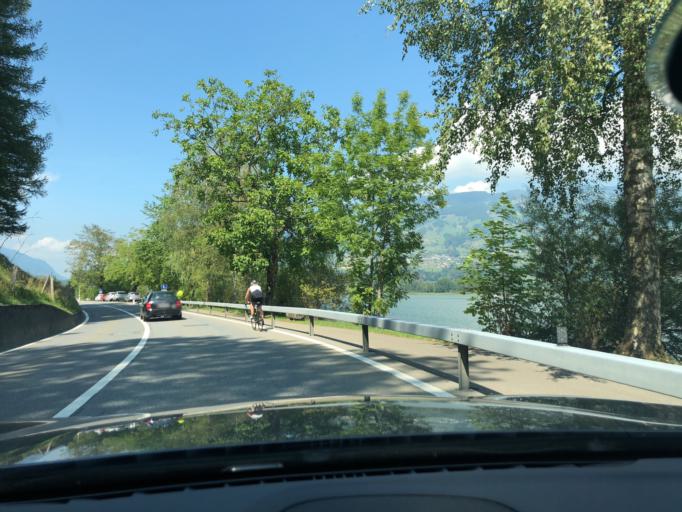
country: CH
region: Schwyz
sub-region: Bezirk Schwyz
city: Steinen
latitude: 47.0296
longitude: 8.6030
